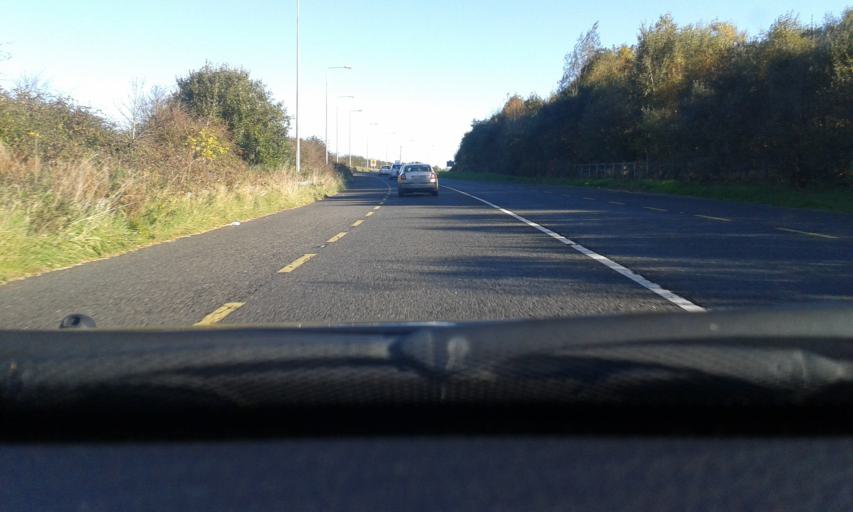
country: IE
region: Leinster
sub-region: Kildare
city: Monasterevin
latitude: 53.1450
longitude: -7.0210
